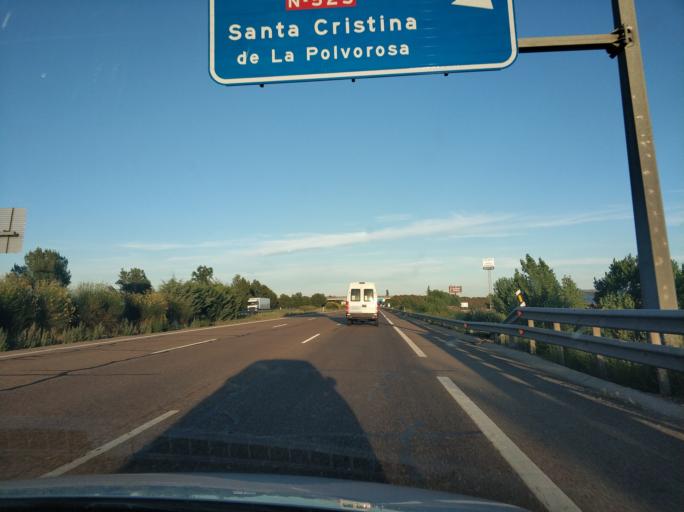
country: ES
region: Castille and Leon
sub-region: Provincia de Zamora
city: Villanueva de Azoague
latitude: 41.9947
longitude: -5.6464
